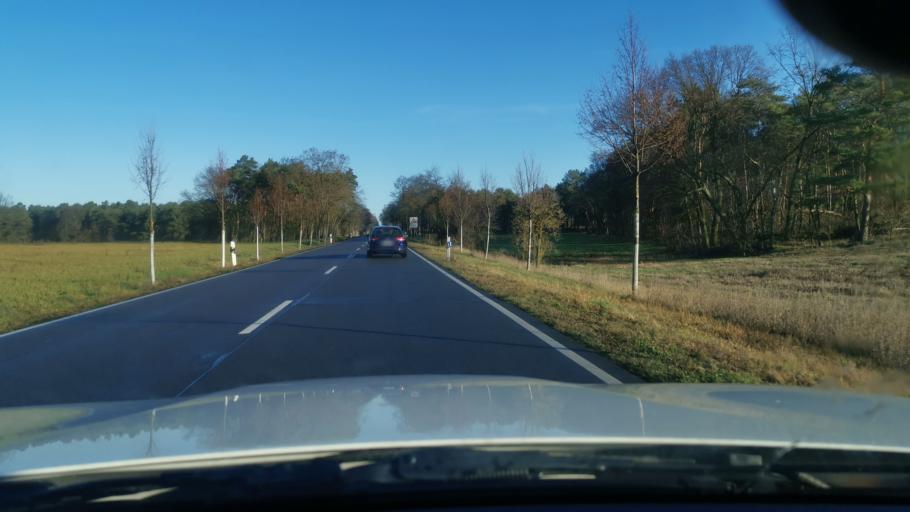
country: DE
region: Saxony-Anhalt
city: Abtsdorf
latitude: 51.9174
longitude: 12.6945
